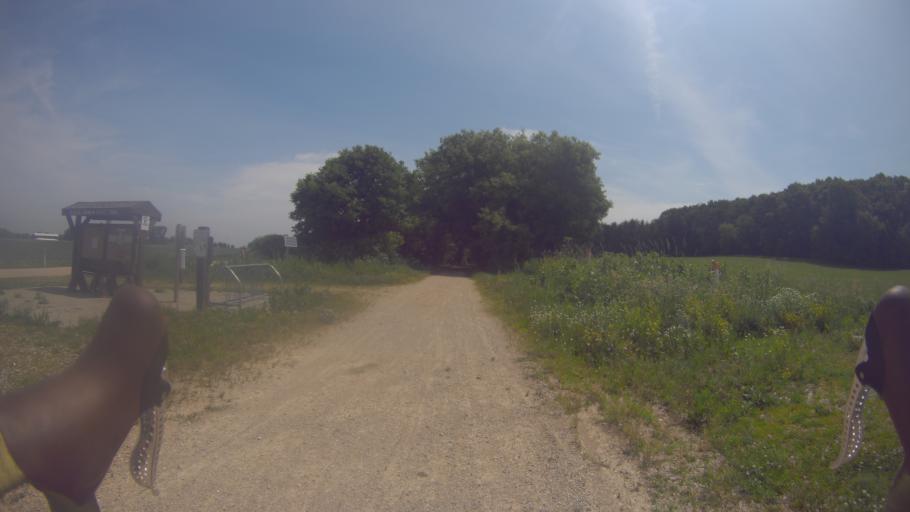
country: US
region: Wisconsin
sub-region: Jefferson County
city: Lake Mills
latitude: 43.0651
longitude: -88.9577
